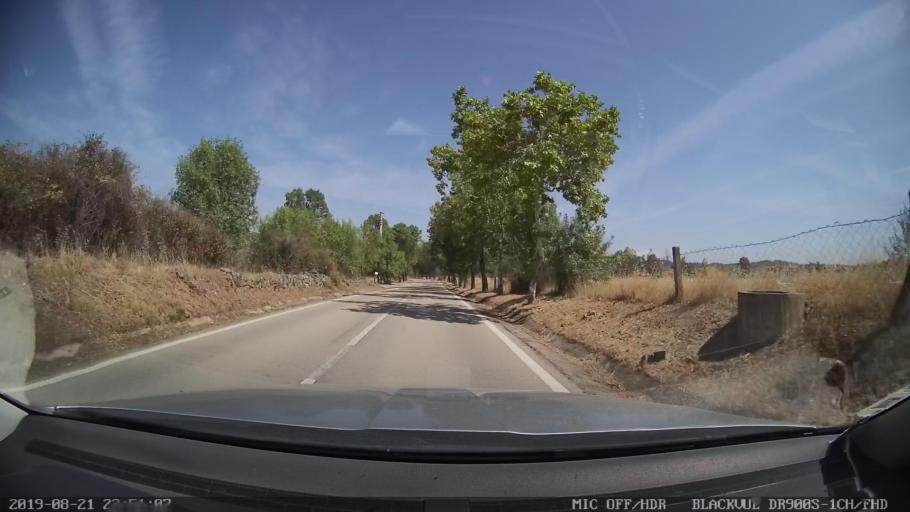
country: PT
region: Castelo Branco
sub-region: Idanha-A-Nova
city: Idanha-a-Nova
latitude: 39.8979
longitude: -7.2356
